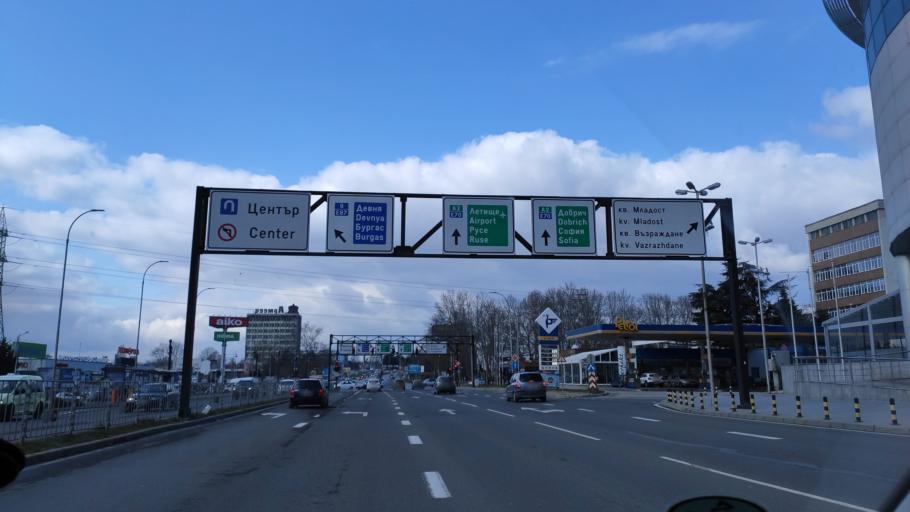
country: BG
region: Varna
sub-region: Obshtina Varna
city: Varna
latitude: 43.2217
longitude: 27.8761
